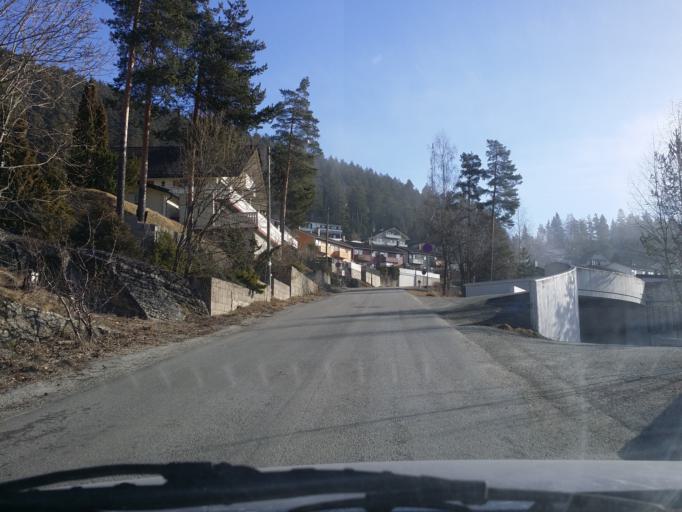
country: NO
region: Buskerud
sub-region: Nedre Eiker
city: Mjondalen
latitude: 59.7622
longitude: 10.0393
